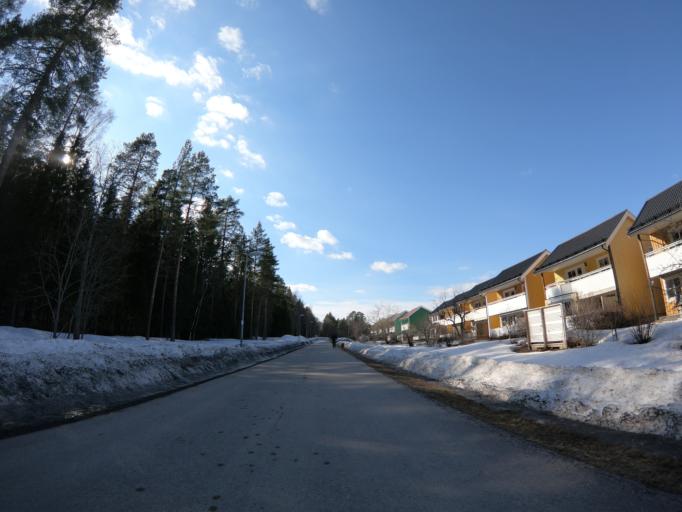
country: SE
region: Vaesterbotten
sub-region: Umea Kommun
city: Ersmark
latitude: 63.8435
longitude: 20.3055
